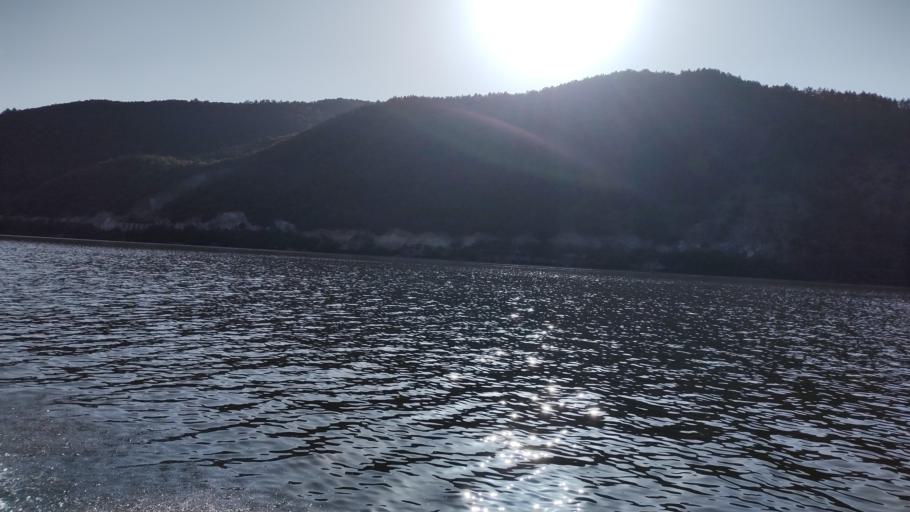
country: RO
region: Mehedinti
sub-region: Comuna Svinita
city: Svinita
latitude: 44.5108
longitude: 22.1984
